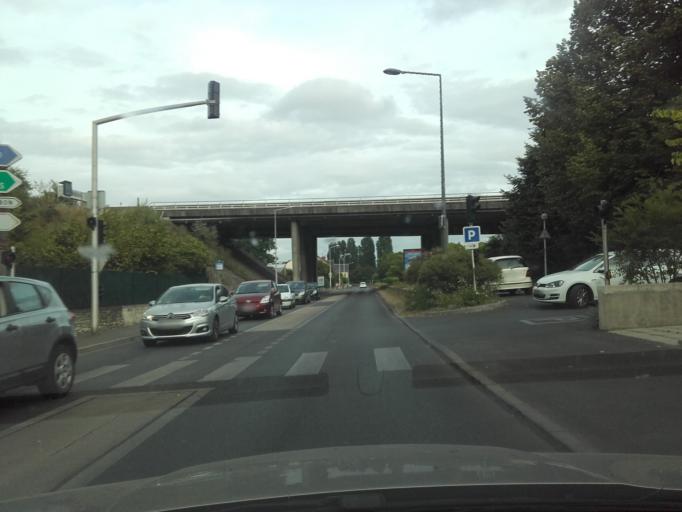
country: FR
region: Centre
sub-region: Departement d'Indre-et-Loire
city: Tours
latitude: 47.4026
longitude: 0.7114
